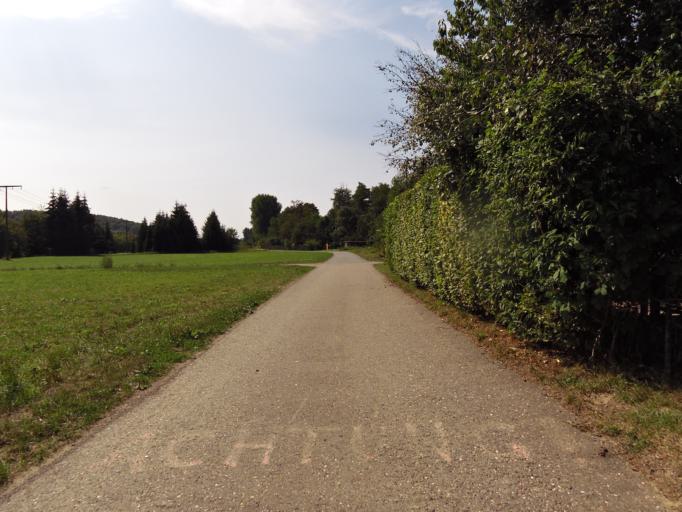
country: DE
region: Baden-Wuerttemberg
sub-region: Karlsruhe Region
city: Eschelbronn
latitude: 49.3243
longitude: 8.8612
